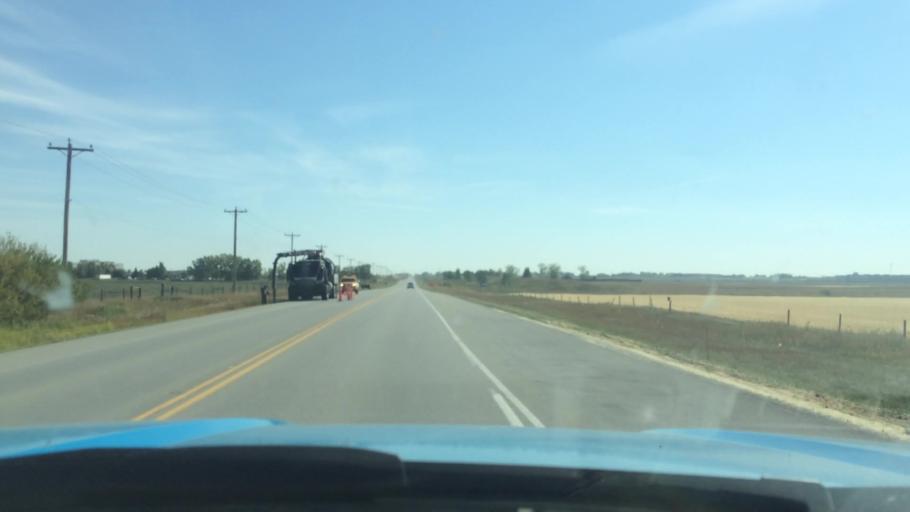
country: CA
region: Alberta
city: Airdrie
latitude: 51.2126
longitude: -113.9562
